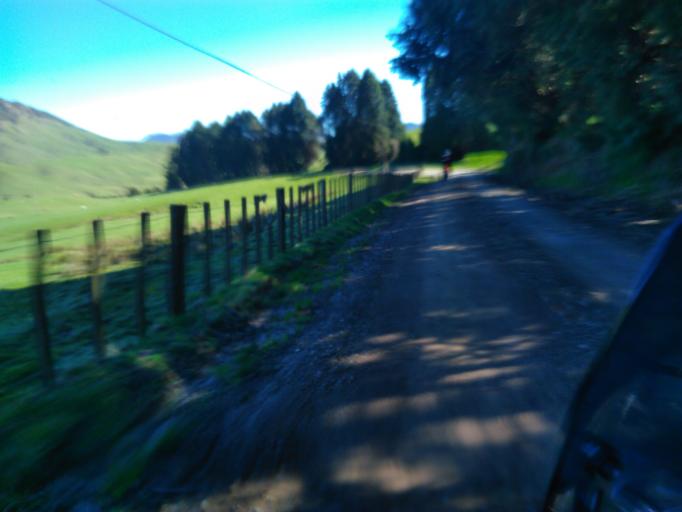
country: NZ
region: Bay of Plenty
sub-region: Opotiki District
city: Opotiki
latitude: -38.3125
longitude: 177.5676
